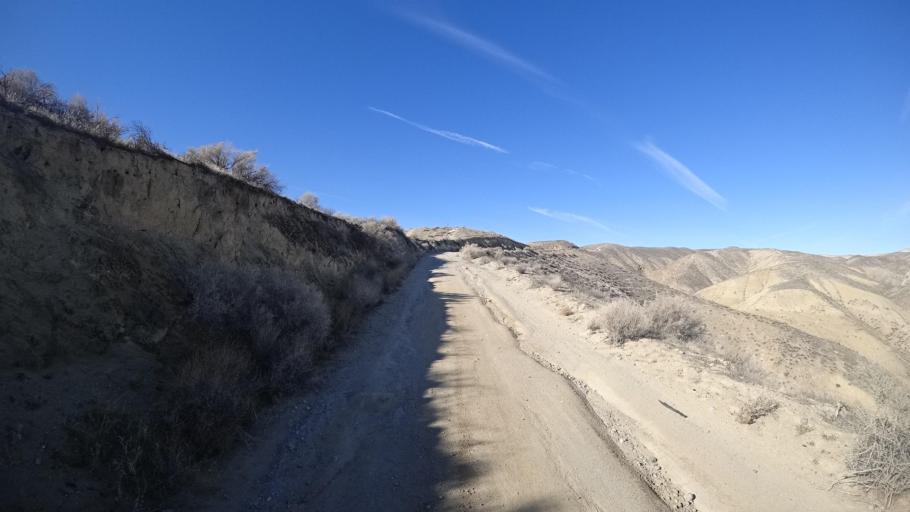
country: US
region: California
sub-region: Kern County
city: Maricopa
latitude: 35.0124
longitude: -119.4636
